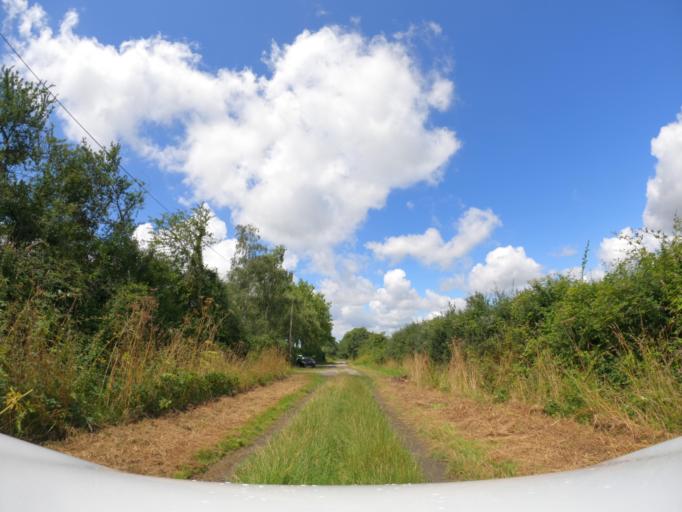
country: FR
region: Pays de la Loire
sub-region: Departement de la Loire-Atlantique
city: Saint-Mars-du-Desert
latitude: 47.3930
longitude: -1.4168
